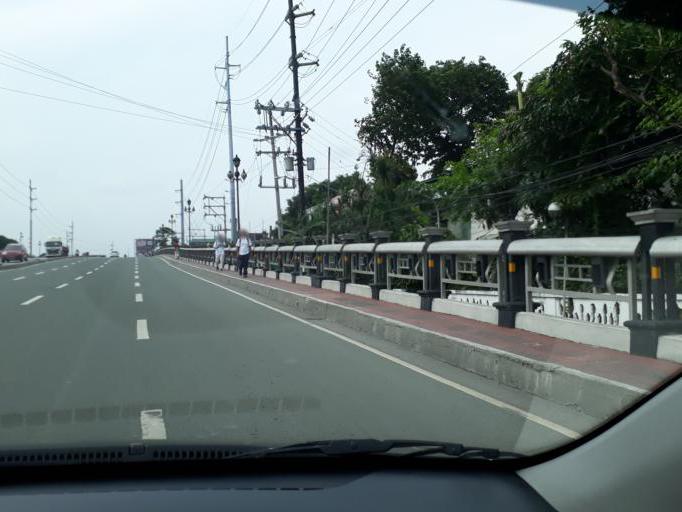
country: PH
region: Metro Manila
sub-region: City of Manila
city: Quiapo
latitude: 14.5935
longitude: 121.0017
